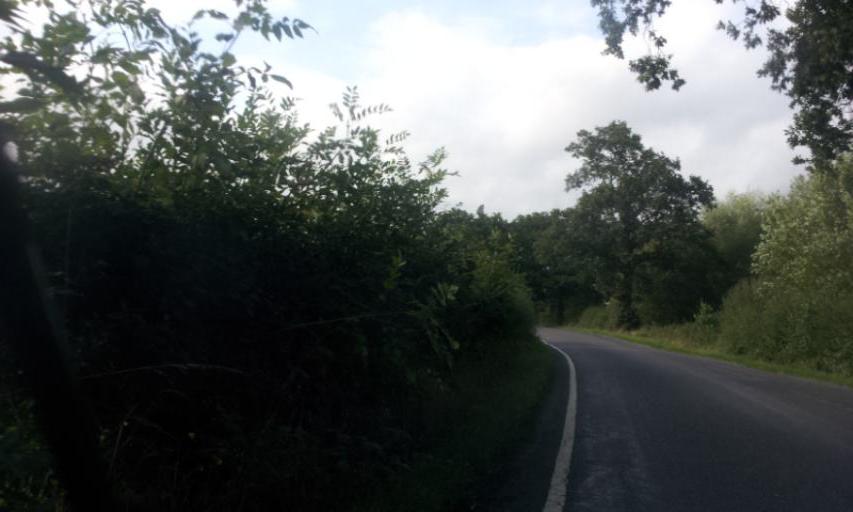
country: GB
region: England
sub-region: Kent
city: Hadlow
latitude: 51.1995
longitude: 0.3311
